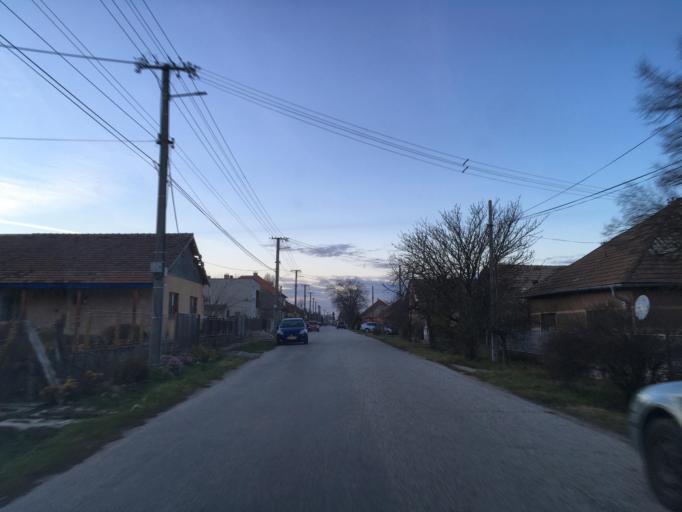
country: SK
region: Nitriansky
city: Svodin
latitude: 47.8666
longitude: 18.4700
